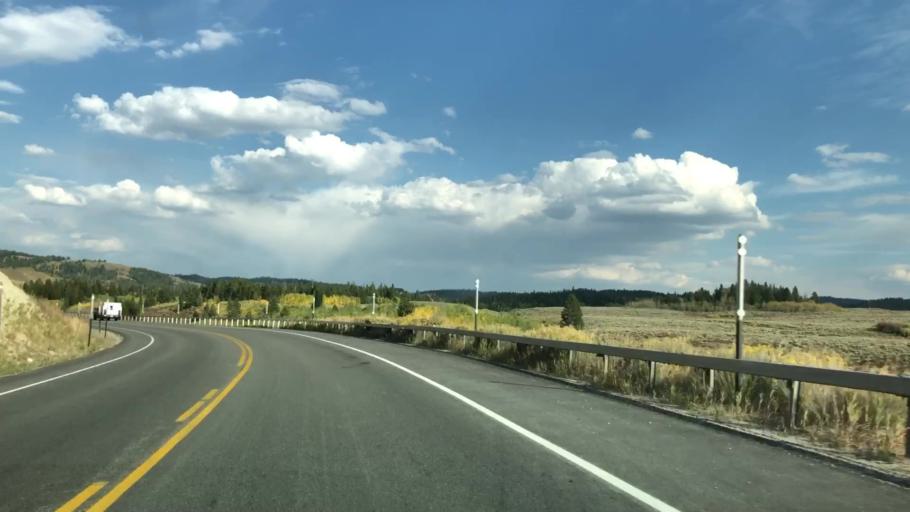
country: US
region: Wyoming
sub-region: Sublette County
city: Pinedale
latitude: 43.1485
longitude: -110.2667
